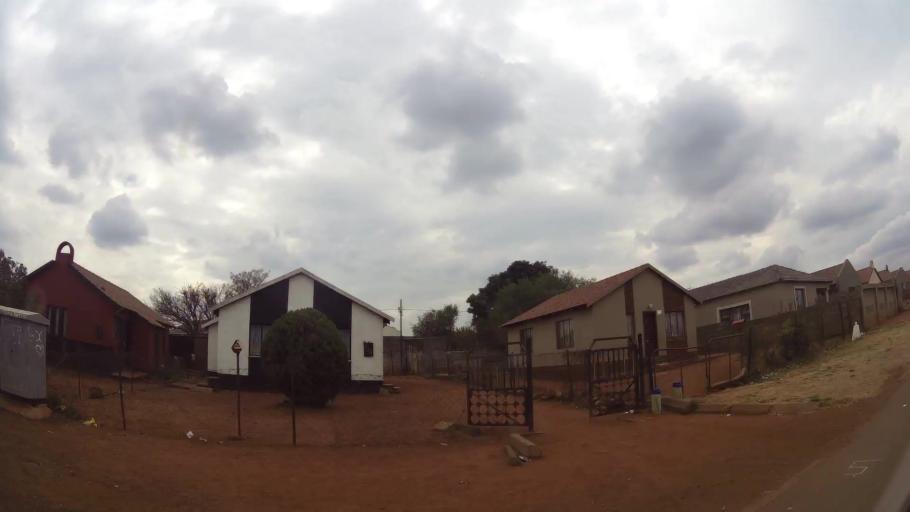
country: ZA
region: Gauteng
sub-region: Ekurhuleni Metropolitan Municipality
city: Germiston
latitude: -26.3833
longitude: 28.1237
